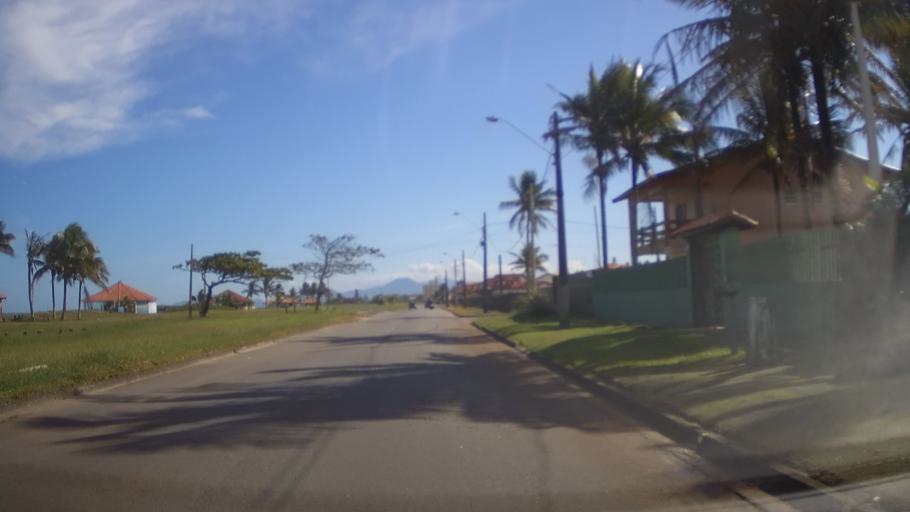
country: BR
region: Sao Paulo
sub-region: Itanhaem
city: Itanhaem
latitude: -24.2089
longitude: -46.8321
